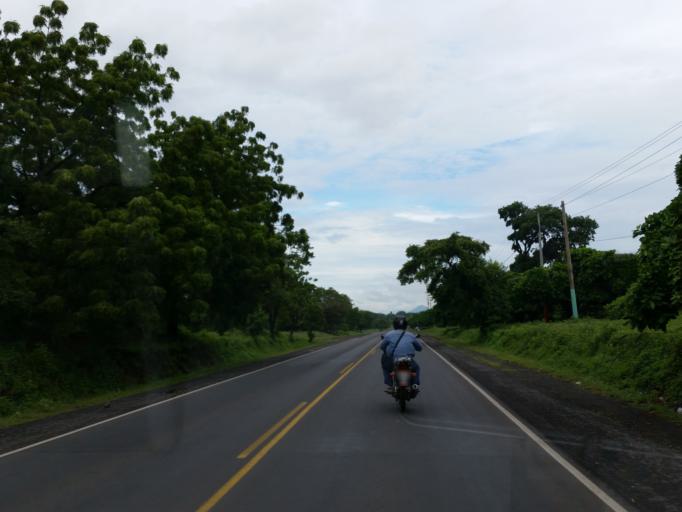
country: NI
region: Managua
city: Ciudad Sandino
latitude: 12.2273
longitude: -86.4131
